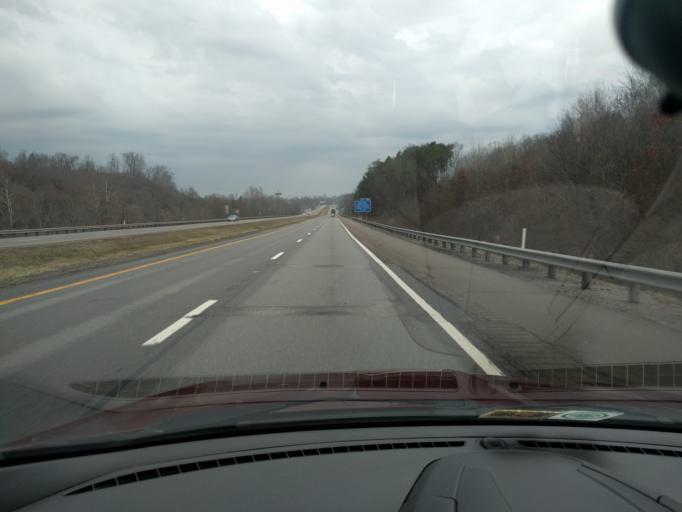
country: US
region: West Virginia
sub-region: Wood County
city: Williamstown
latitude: 39.3809
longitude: -81.4398
